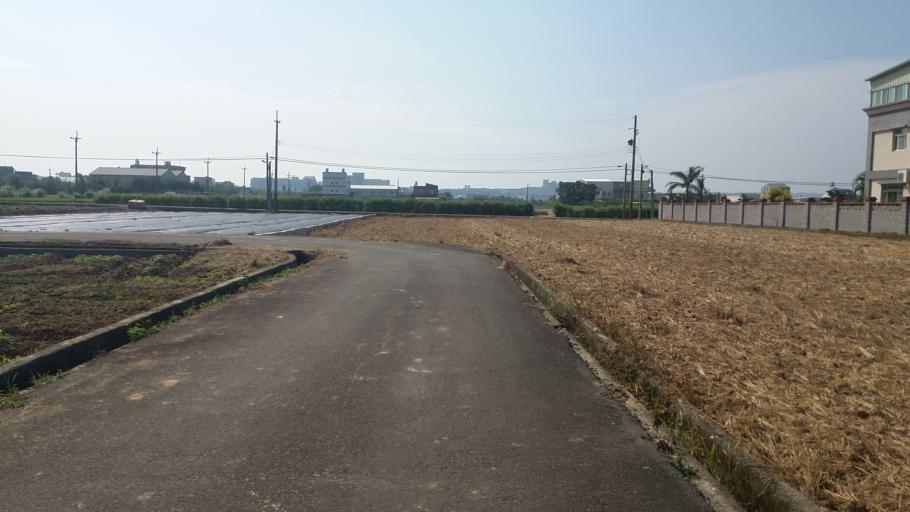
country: TW
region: Taiwan
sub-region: Hsinchu
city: Zhubei
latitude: 24.8960
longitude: 121.0164
